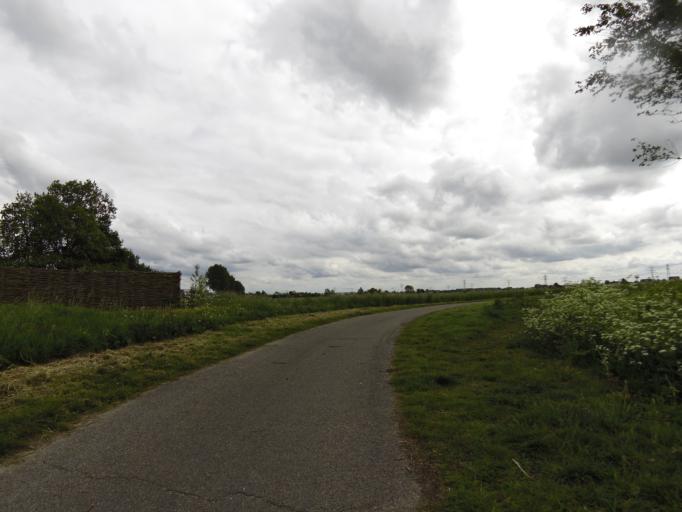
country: NL
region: South Holland
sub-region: Gemeente Brielle
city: Brielle
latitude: 51.8933
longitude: 4.1719
